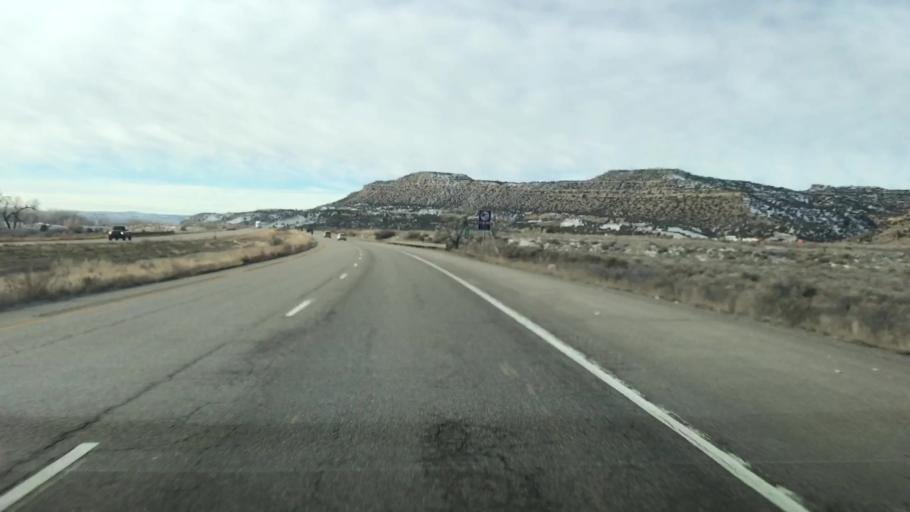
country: US
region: Colorado
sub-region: Garfield County
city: Parachute
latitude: 39.3509
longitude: -108.1808
